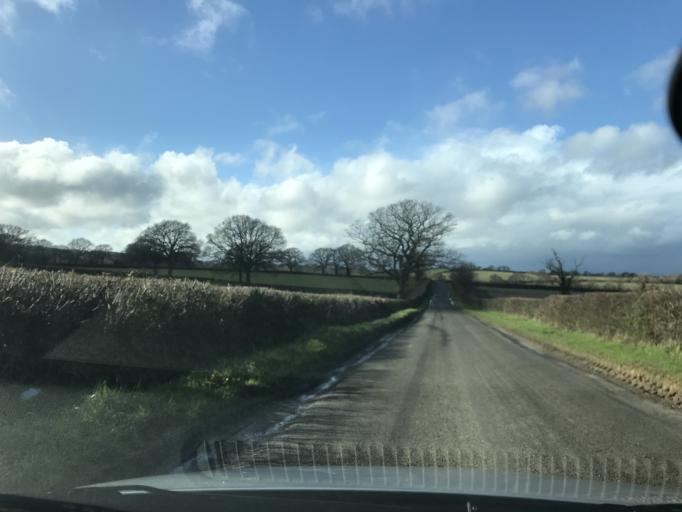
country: GB
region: England
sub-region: Somerset
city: Chard
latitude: 50.9402
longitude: -2.9895
